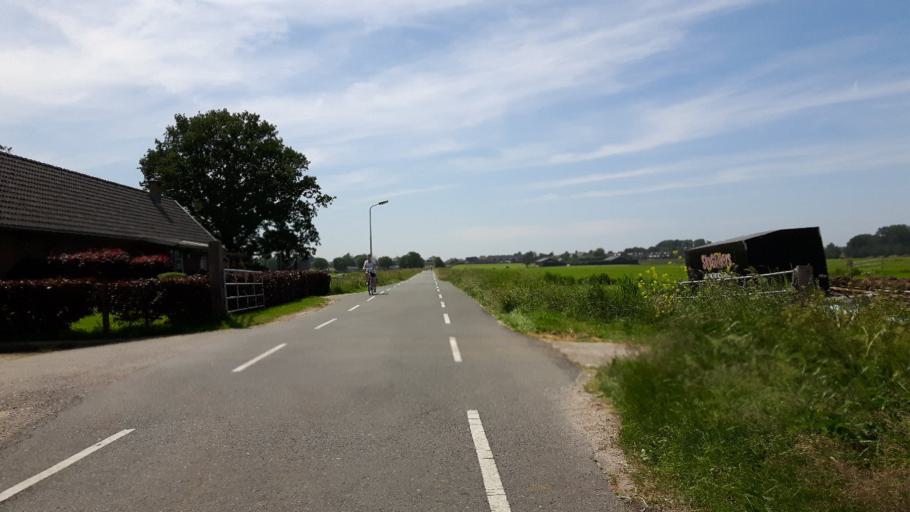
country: NL
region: South Holland
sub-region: Gemeente Nieuwkoop
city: Nieuwkoop
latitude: 52.1410
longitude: 4.7420
